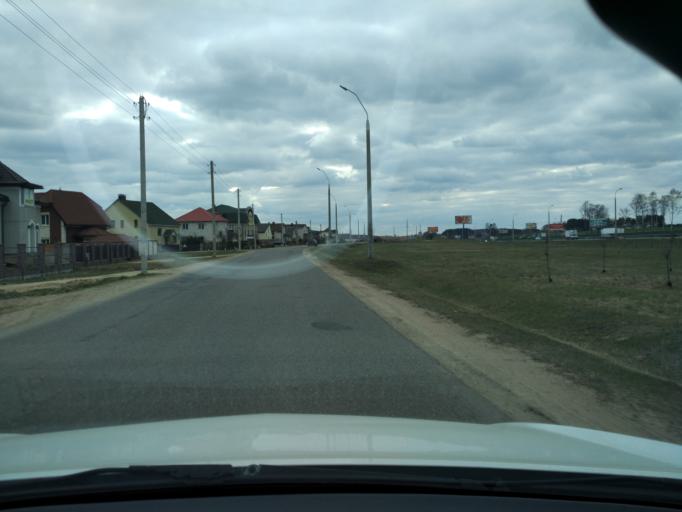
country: BY
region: Minsk
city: Bal'shavik
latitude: 53.9707
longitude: 27.5803
